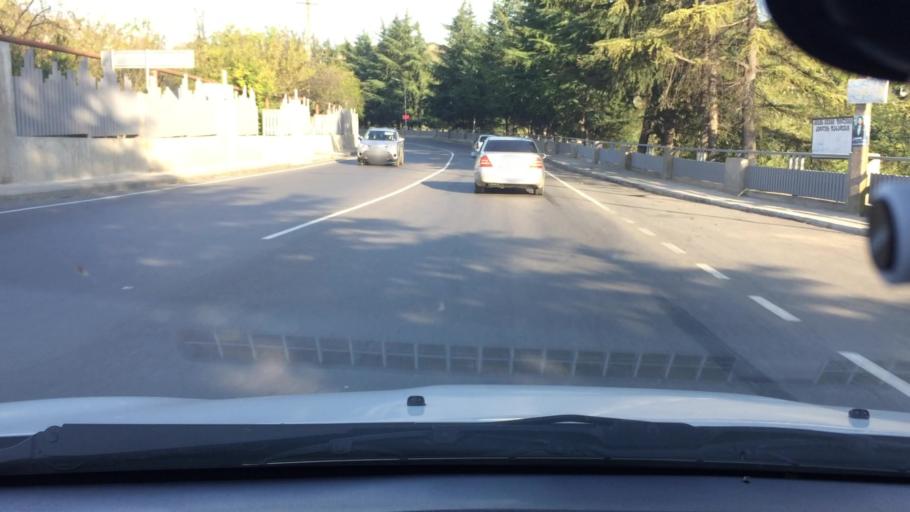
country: GE
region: Imereti
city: Zestap'oni
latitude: 42.1063
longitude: 43.0523
